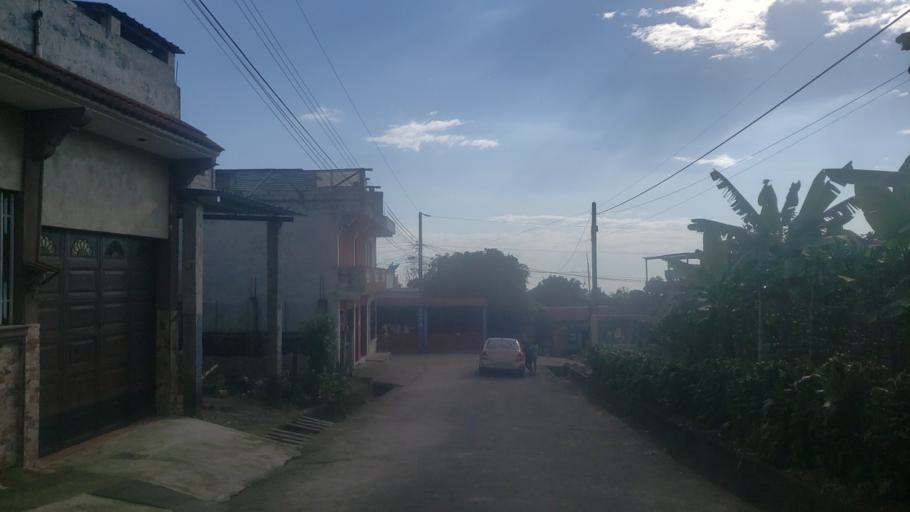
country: GT
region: Quetzaltenango
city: El Palmar
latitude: 14.6440
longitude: -91.5595
